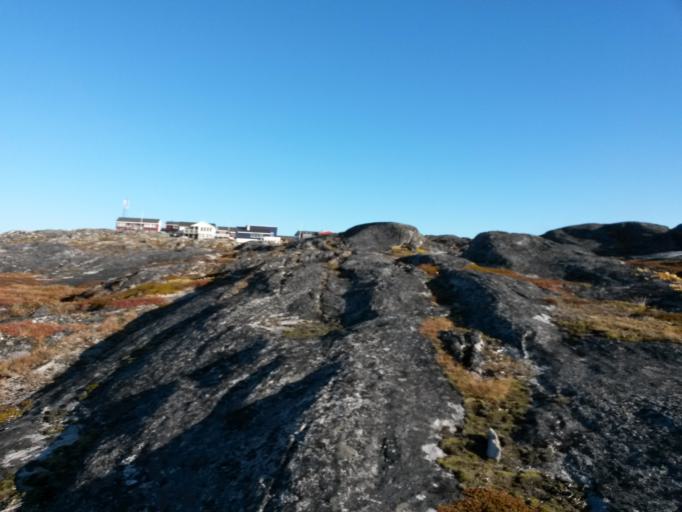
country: GL
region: Sermersooq
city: Nuuk
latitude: 64.1736
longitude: -51.7144
